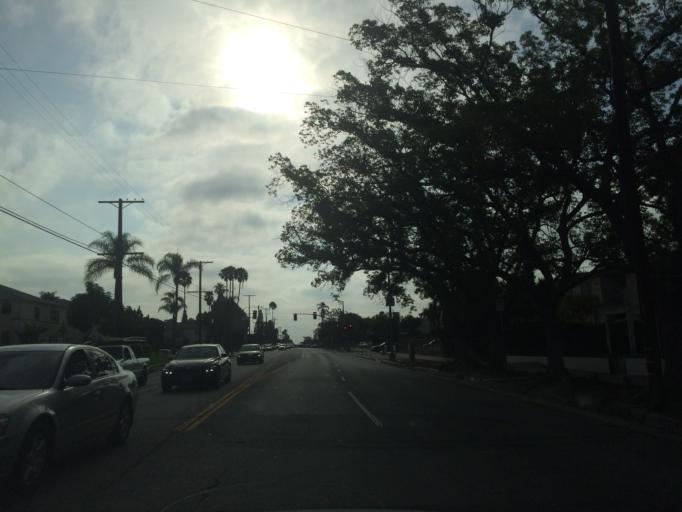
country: US
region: California
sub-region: Los Angeles County
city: View Park-Windsor Hills
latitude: 34.0323
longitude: -118.3245
